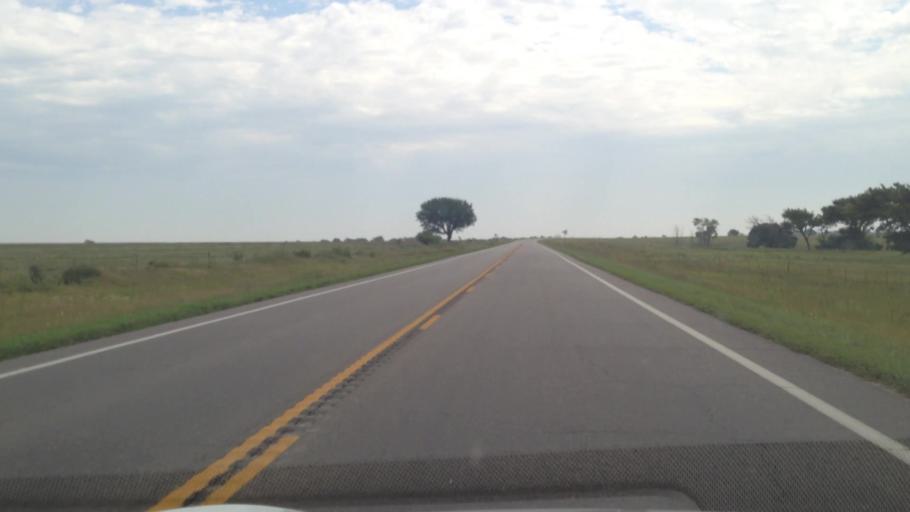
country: US
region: Kansas
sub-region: Bourbon County
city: Fort Scott
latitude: 37.8845
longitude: -95.0190
